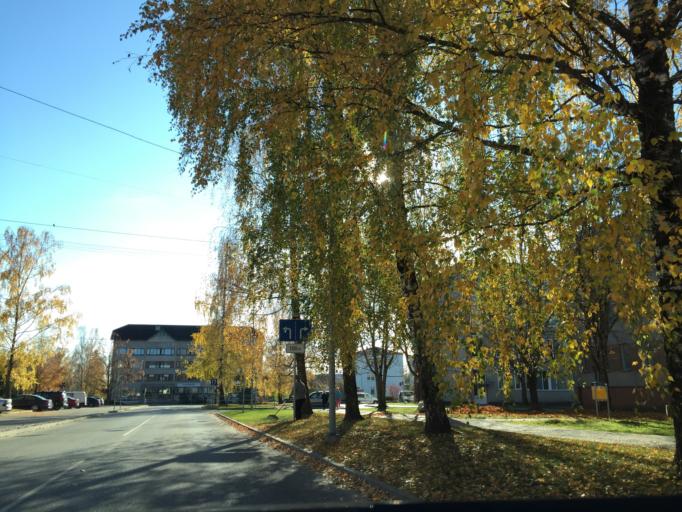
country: LV
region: Aizkraukles Rajons
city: Aizkraukle
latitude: 56.6019
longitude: 25.2548
